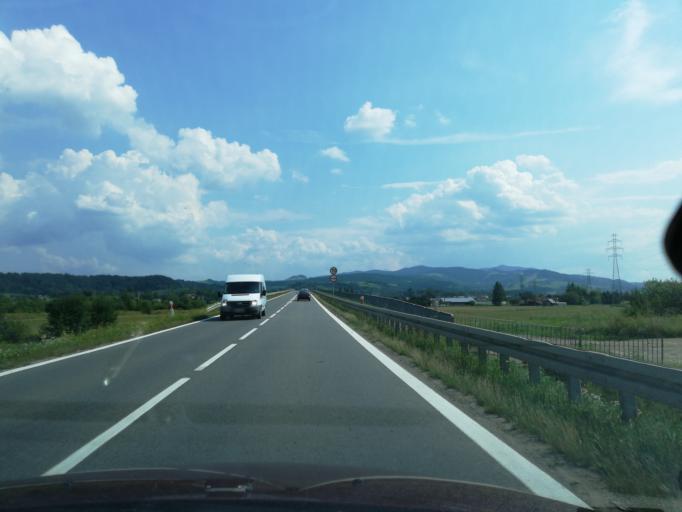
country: PL
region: Lesser Poland Voivodeship
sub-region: Powiat nowosadecki
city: Stary Sacz
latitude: 49.5751
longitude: 20.6437
